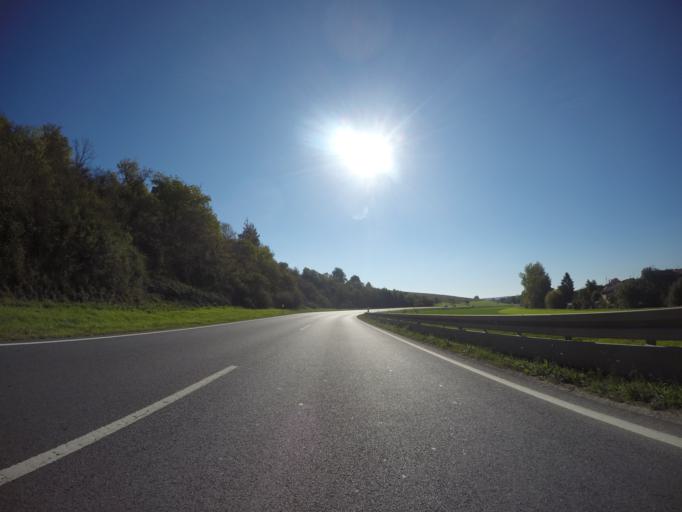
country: DE
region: Bavaria
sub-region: Regierungsbezirk Unterfranken
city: Greussenheim
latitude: 49.7853
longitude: 9.7708
